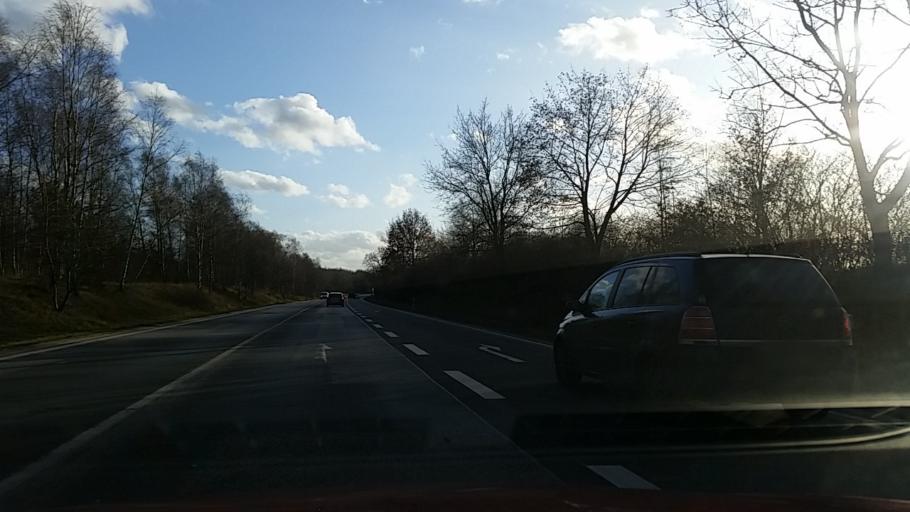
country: DE
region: Schleswig-Holstein
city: Glinde
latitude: 53.5542
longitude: 10.2334
